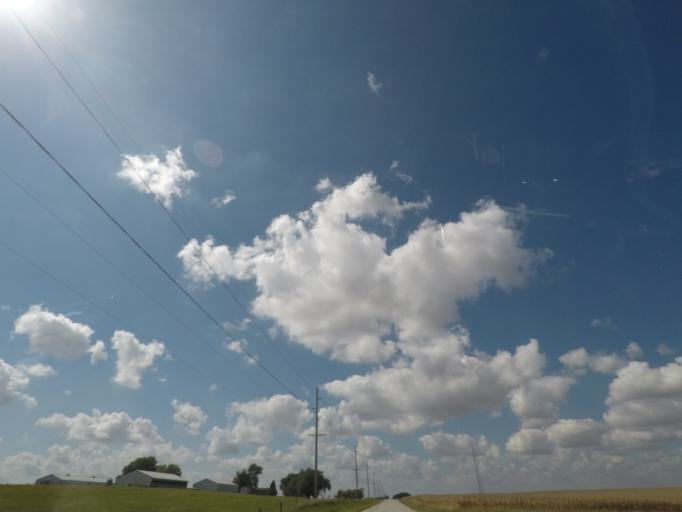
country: US
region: Iowa
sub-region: Story County
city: Nevada
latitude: 42.0343
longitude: -93.3788
